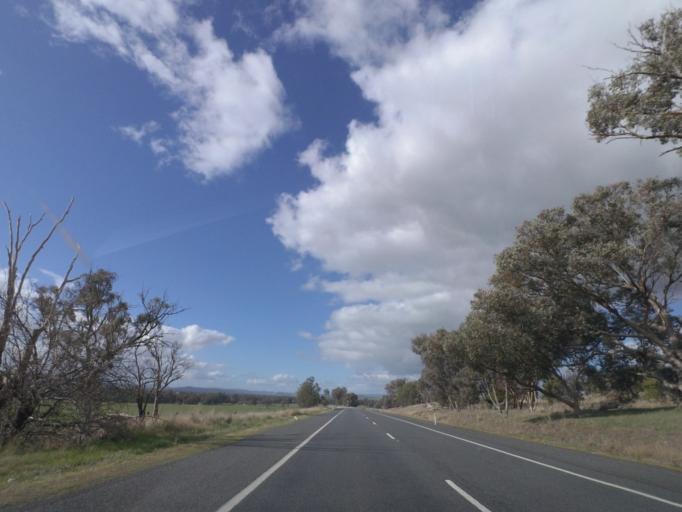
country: AU
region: New South Wales
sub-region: Greater Hume Shire
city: Holbrook
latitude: -35.6716
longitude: 147.4010
